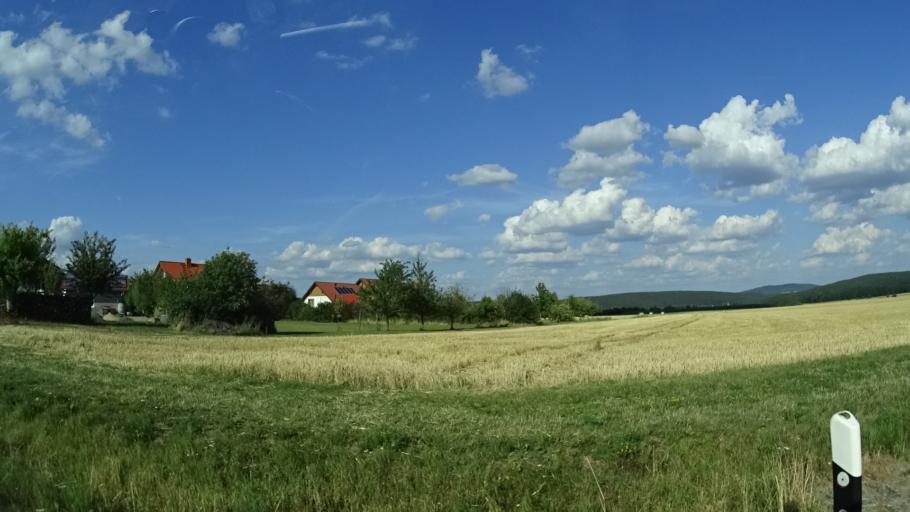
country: DE
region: Bavaria
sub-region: Regierungsbezirk Unterfranken
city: Oberelsbach
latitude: 50.4202
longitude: 10.0953
